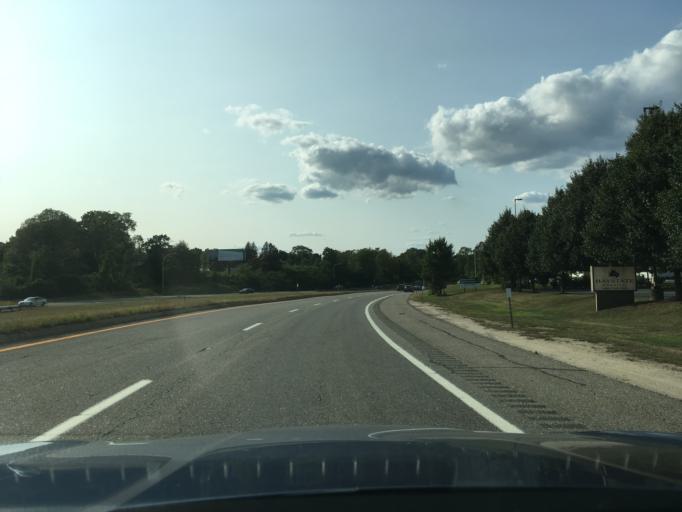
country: US
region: Massachusetts
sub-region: Bristol County
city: Seekonk
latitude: 41.7929
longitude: -71.3493
